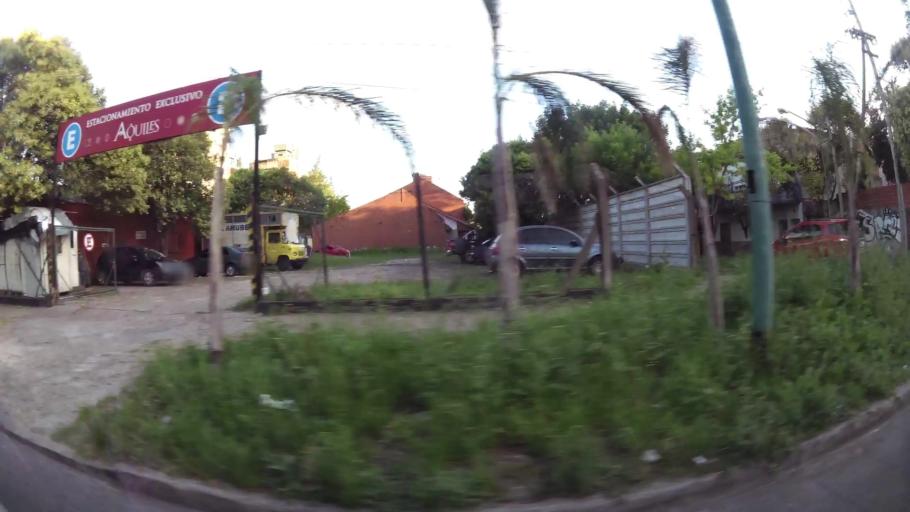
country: AR
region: Buenos Aires
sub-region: Partido de General San Martin
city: General San Martin
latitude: -34.5452
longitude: -58.4982
